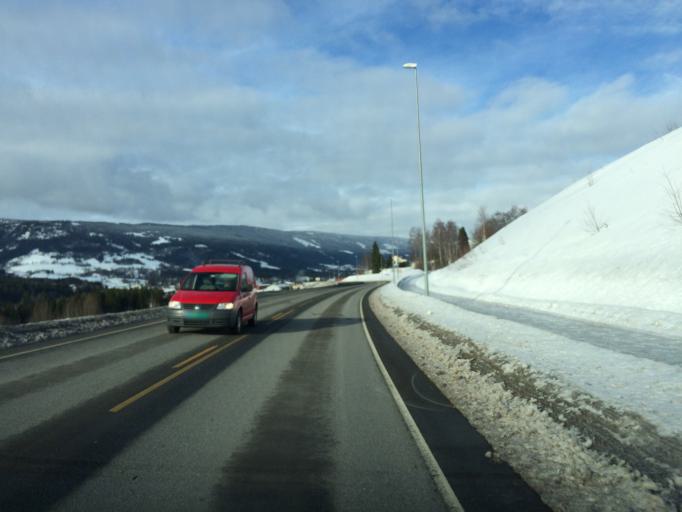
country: NO
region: Oppland
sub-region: Gausdal
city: Segalstad bru
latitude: 61.2216
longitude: 10.2408
